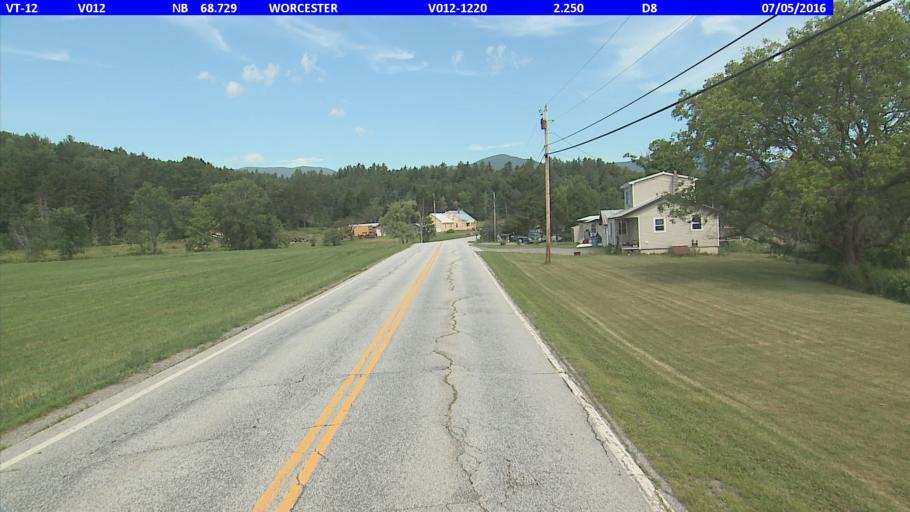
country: US
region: Vermont
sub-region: Washington County
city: Montpelier
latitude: 44.3810
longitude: -72.5508
